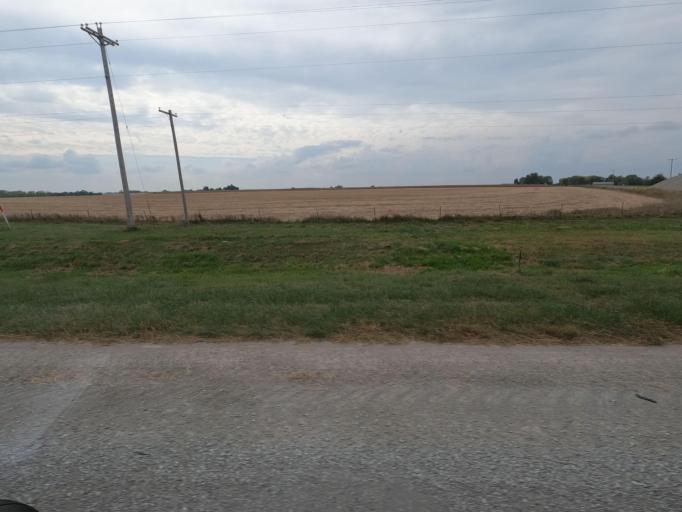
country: US
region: Iowa
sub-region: Jasper County
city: Monroe
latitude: 41.4505
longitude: -93.0246
